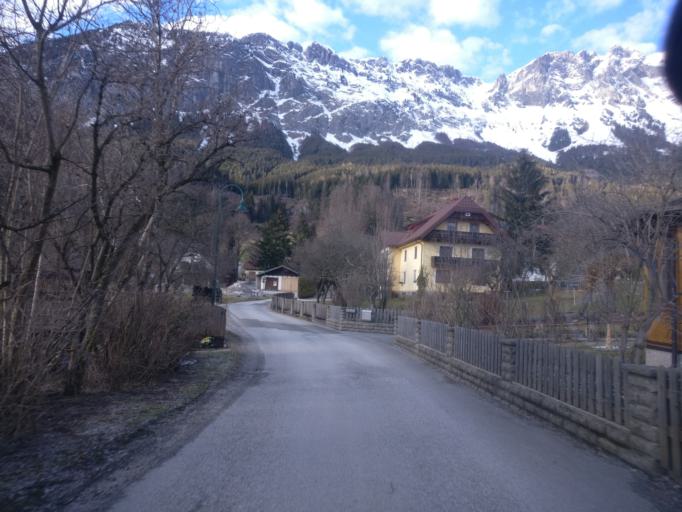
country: AT
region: Styria
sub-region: Politischer Bezirk Liezen
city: Sankt Martin am Grimming
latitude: 47.4864
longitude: 13.9725
